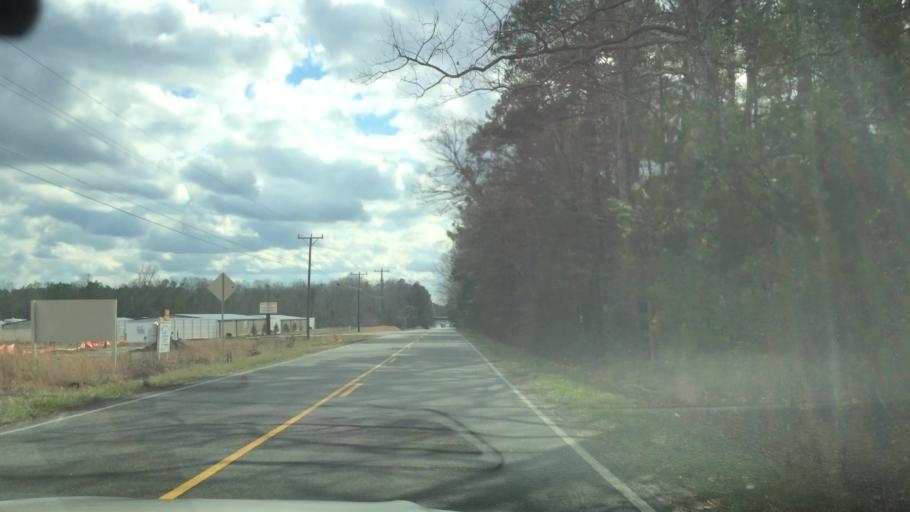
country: US
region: Virginia
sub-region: New Kent County
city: New Kent
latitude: 37.5016
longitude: -77.0204
